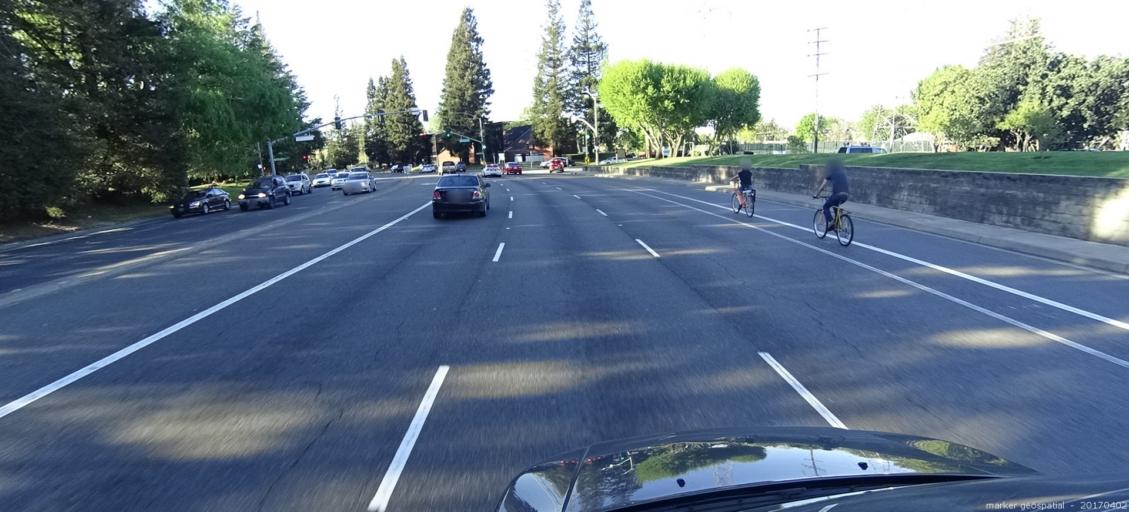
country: US
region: California
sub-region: Sacramento County
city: Arden-Arcade
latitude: 38.5687
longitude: -121.4089
